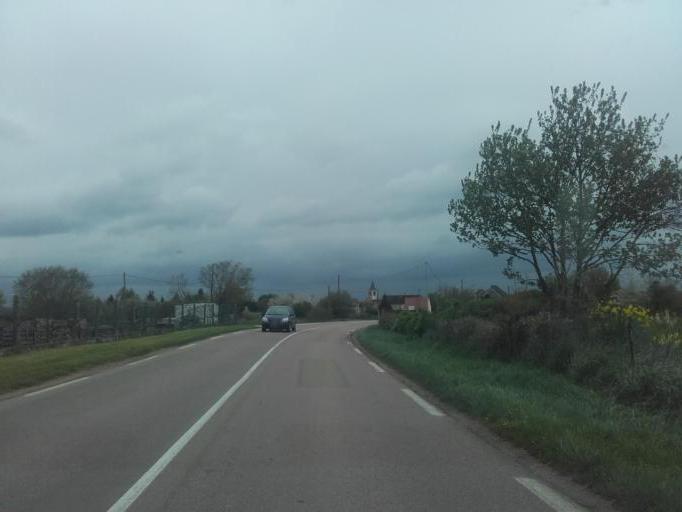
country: FR
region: Bourgogne
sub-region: Departement de l'Yonne
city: Joux-la-Ville
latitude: 47.6678
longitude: 3.8780
